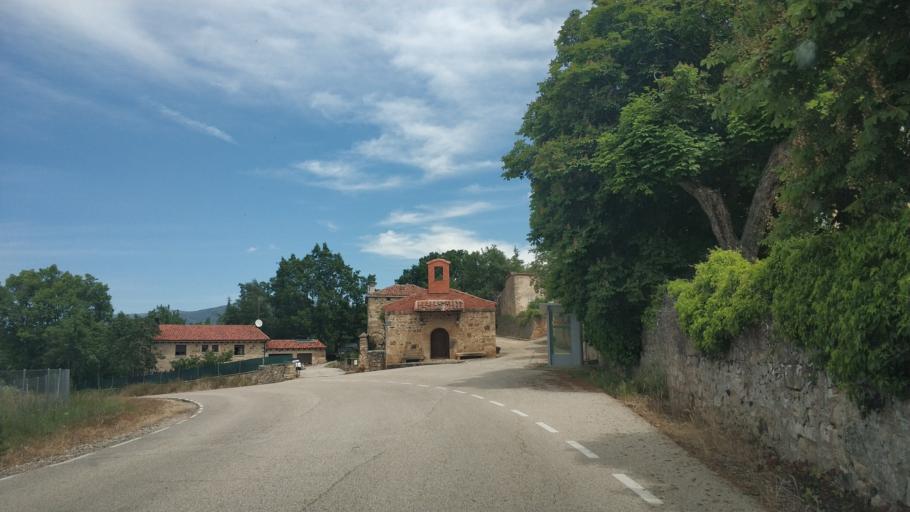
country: ES
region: Castille and Leon
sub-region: Provincia de Soria
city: Sotillo del Rincon
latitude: 41.8963
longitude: -2.6378
